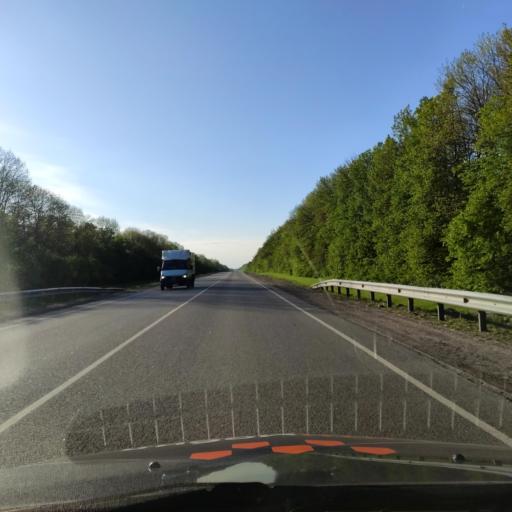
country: RU
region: Lipetsk
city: Yelets
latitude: 52.5759
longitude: 38.6473
